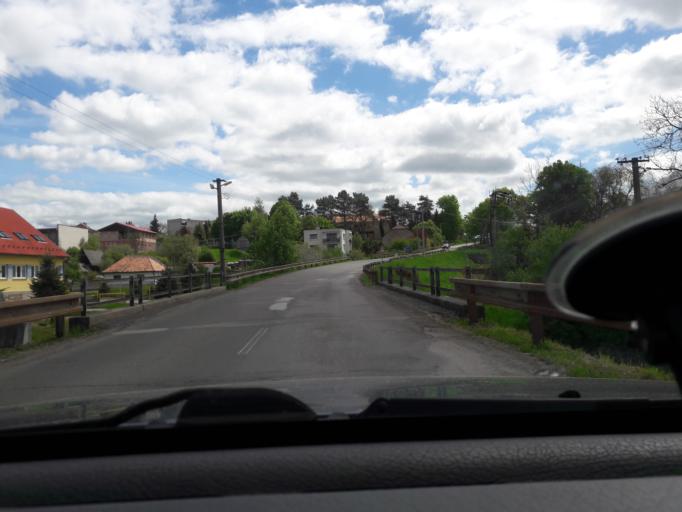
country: SK
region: Banskobystricky
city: Krupina
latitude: 48.3202
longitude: 19.0891
